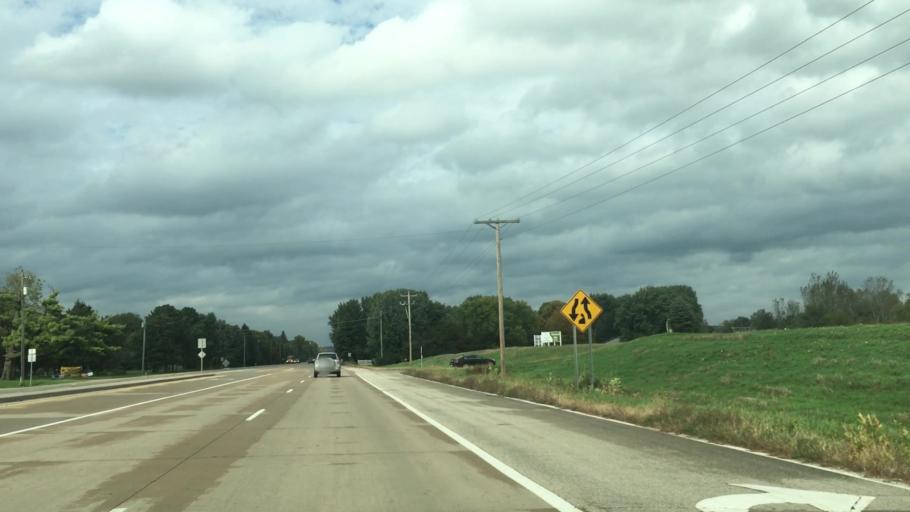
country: US
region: Minnesota
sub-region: Olmsted County
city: Rochester
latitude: 43.9763
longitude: -92.4394
